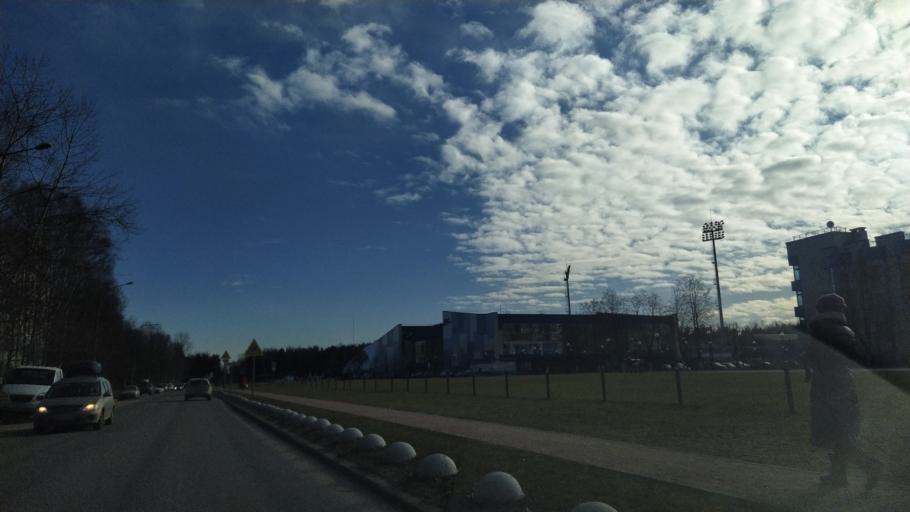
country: RU
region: Leningrad
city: Akademicheskoe
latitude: 60.0055
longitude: 30.4085
